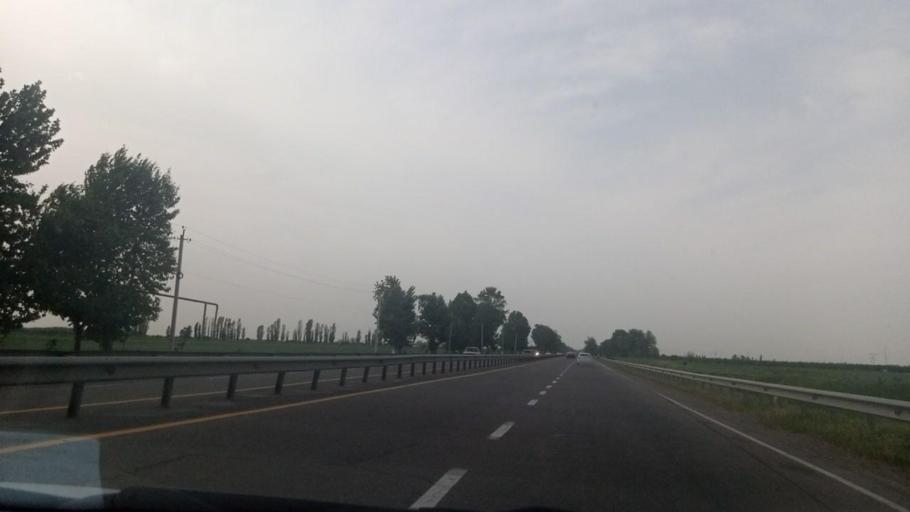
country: UZ
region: Toshkent Shahri
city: Bektemir
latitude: 41.1626
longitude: 69.4195
